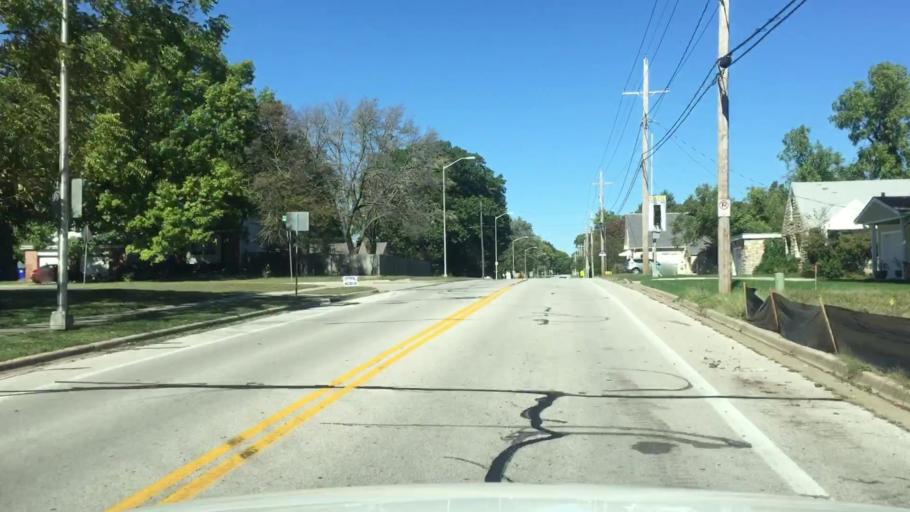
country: US
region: Kansas
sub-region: Johnson County
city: Shawnee
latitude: 39.0239
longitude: -94.7332
